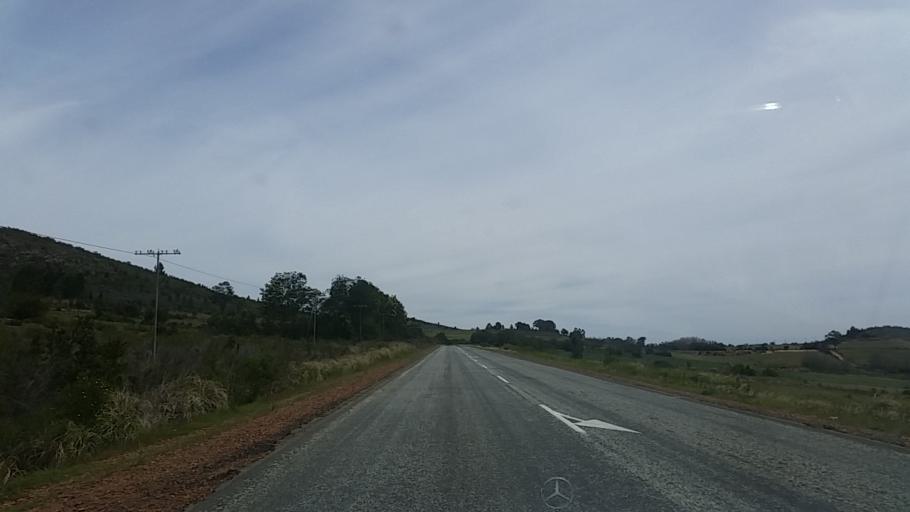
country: ZA
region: Western Cape
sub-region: Eden District Municipality
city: Knysna
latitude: -33.7737
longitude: 22.9143
